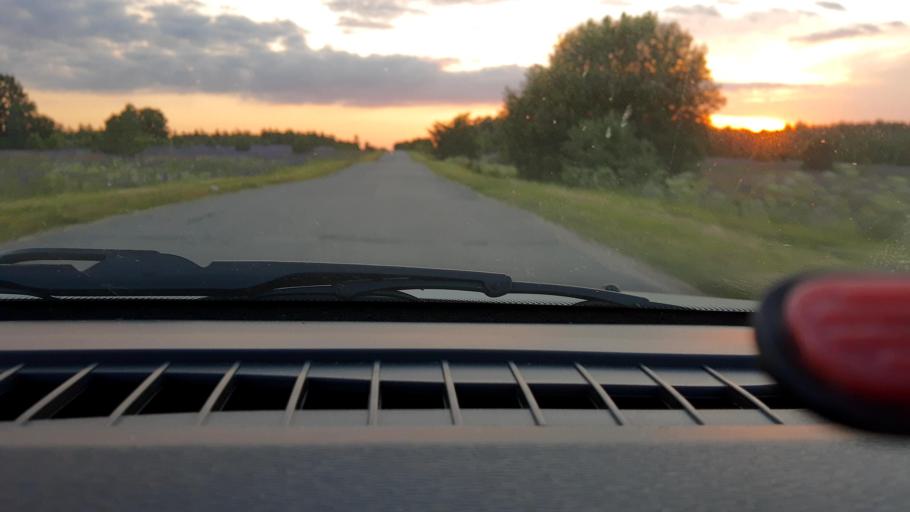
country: RU
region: Nizjnij Novgorod
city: Surovatikha
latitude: 55.8473
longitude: 43.9655
